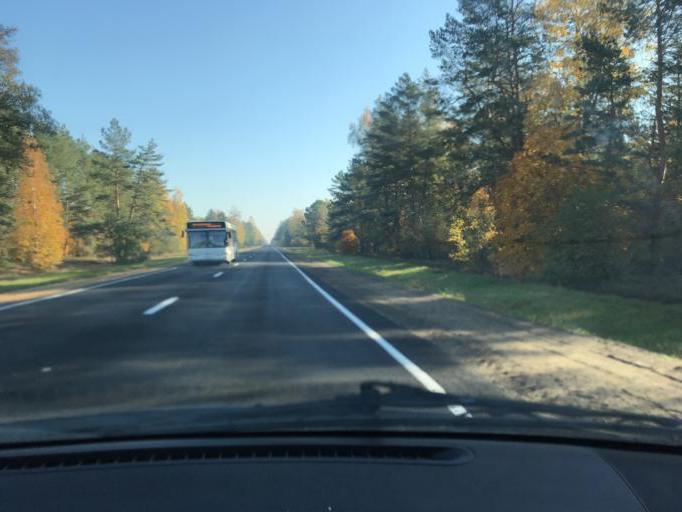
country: BY
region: Brest
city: Baranovichi
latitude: 52.9029
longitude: 25.8859
